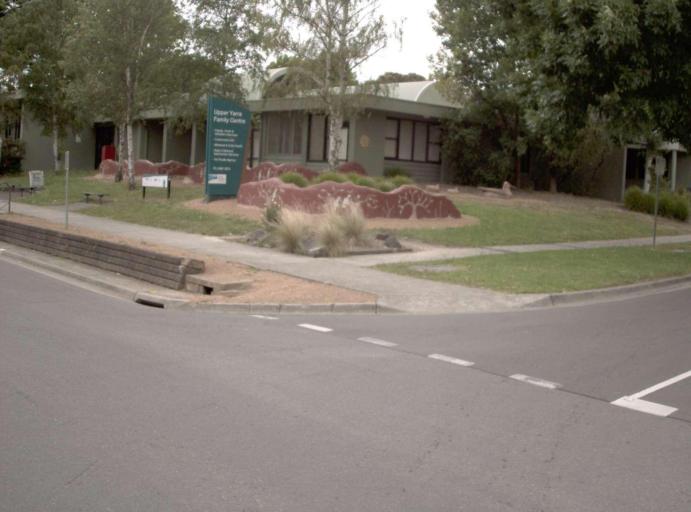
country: AU
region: Victoria
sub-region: Yarra Ranges
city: Yarra Junction
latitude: -37.7817
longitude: 145.6114
